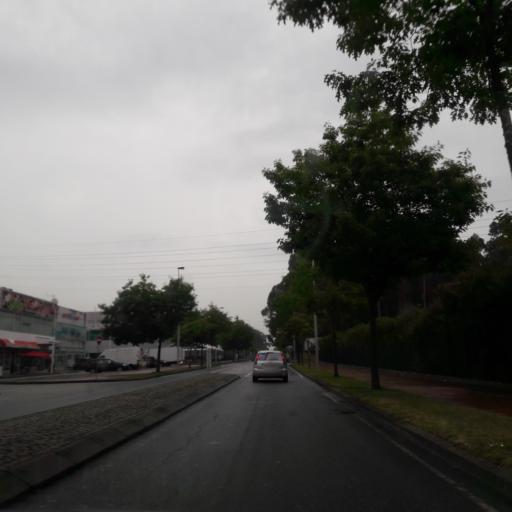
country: PT
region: Porto
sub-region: Vila do Conde
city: Arvore
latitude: 41.3240
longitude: -8.7151
